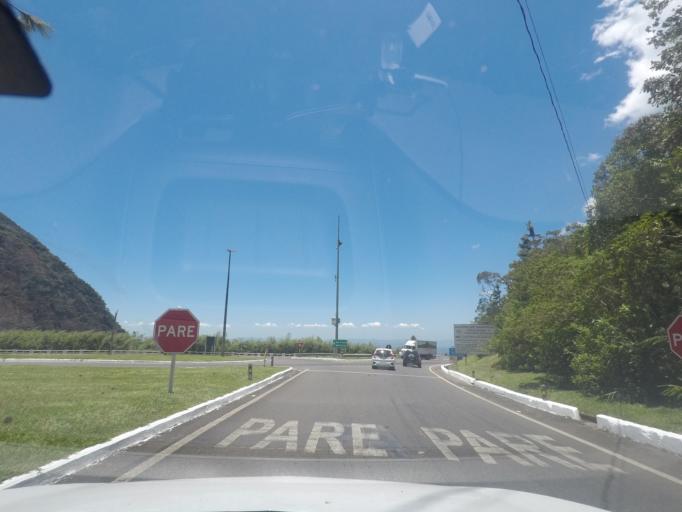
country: BR
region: Rio de Janeiro
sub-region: Teresopolis
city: Teresopolis
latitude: -22.4621
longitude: -42.9878
